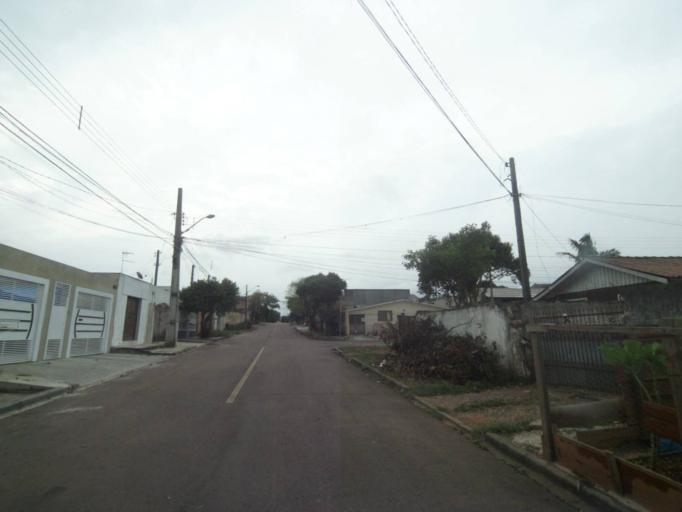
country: BR
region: Parana
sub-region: Sao Jose Dos Pinhais
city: Sao Jose dos Pinhais
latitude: -25.5518
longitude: -49.2620
